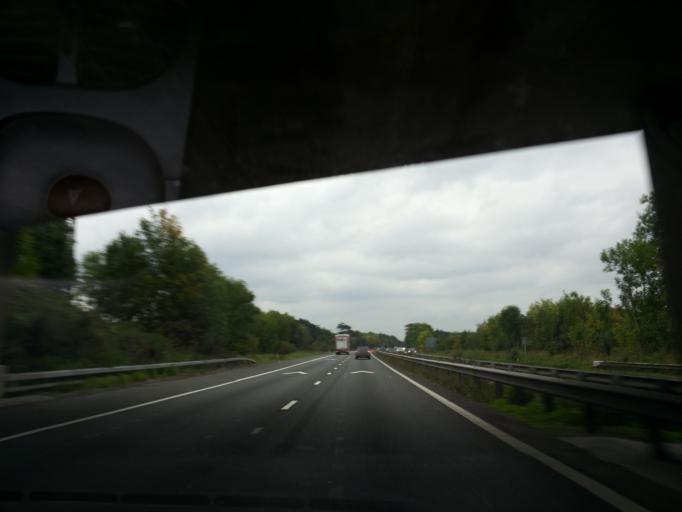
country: GB
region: England
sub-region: Kent
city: Teynham
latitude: 51.2974
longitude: 0.7790
